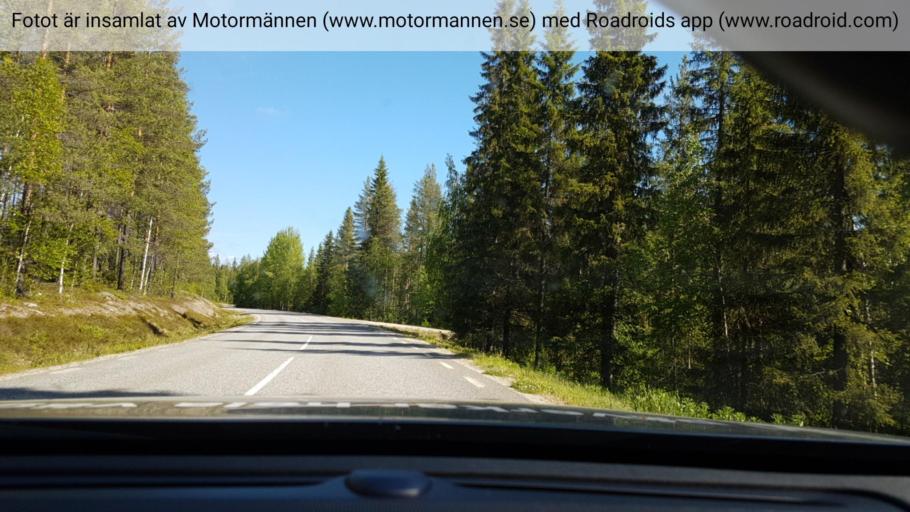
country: SE
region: Vaesterbotten
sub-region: Lycksele Kommun
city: Soderfors
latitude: 64.6211
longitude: 18.2735
